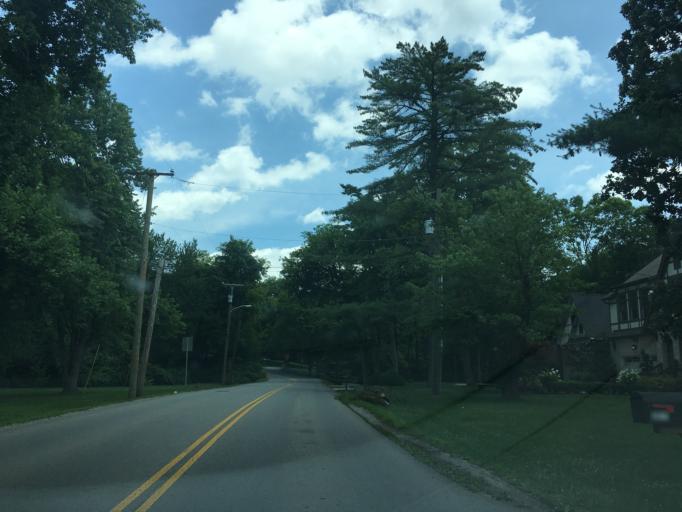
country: US
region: Tennessee
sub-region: Davidson County
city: Belle Meade
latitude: 36.1092
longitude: -86.8215
